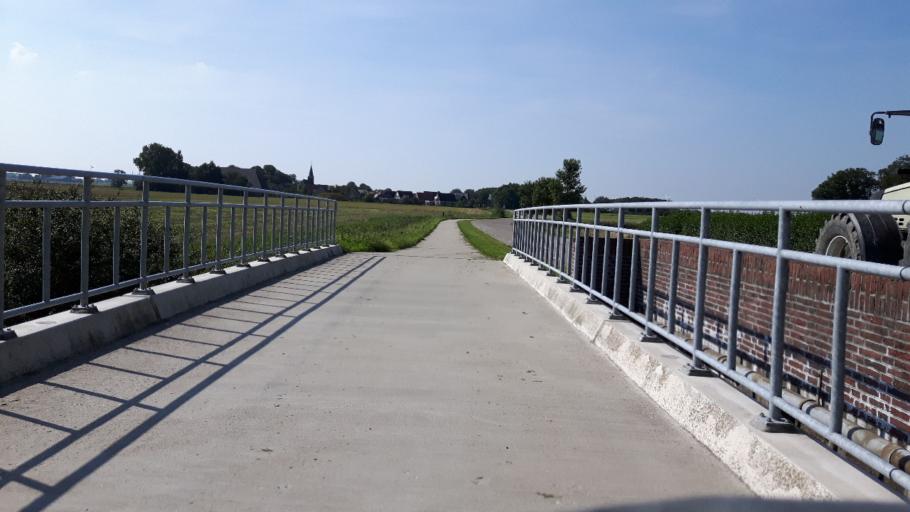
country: NL
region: Friesland
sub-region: Gemeente Franekeradeel
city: Franeker
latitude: 53.2089
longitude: 5.5529
